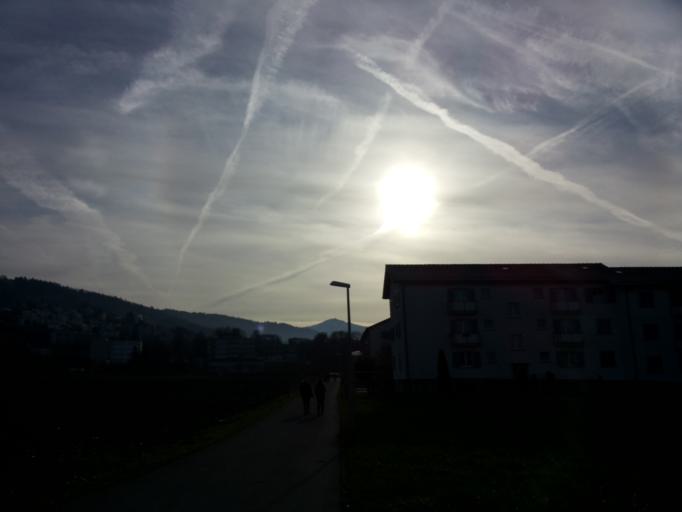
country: CH
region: Zug
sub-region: Zug
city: Zug
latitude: 47.1782
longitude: 8.5239
